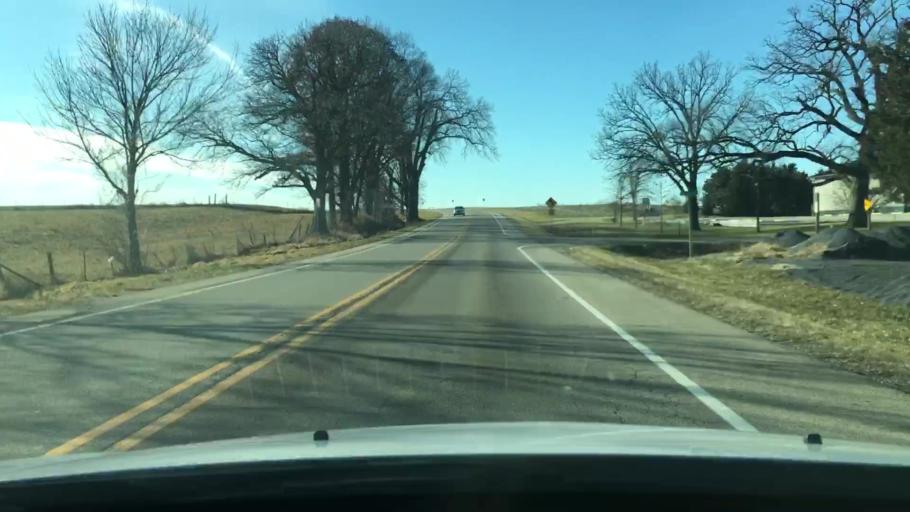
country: US
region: Illinois
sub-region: Woodford County
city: Washburn
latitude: 40.8639
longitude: -89.3299
